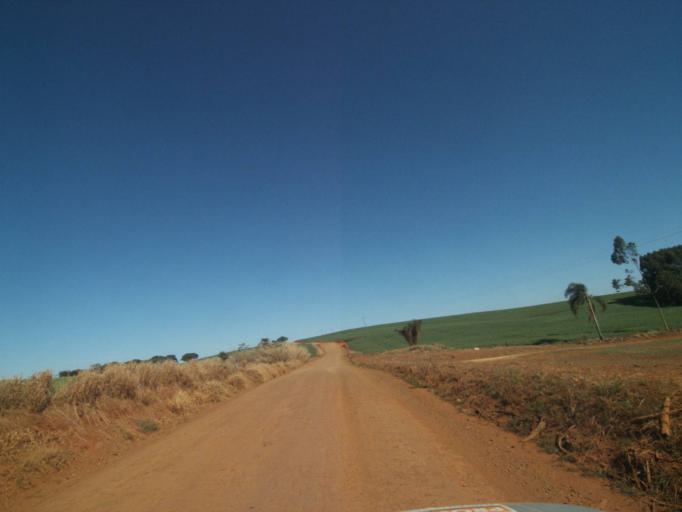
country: BR
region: Parana
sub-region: Tibagi
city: Tibagi
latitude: -24.5990
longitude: -50.6025
